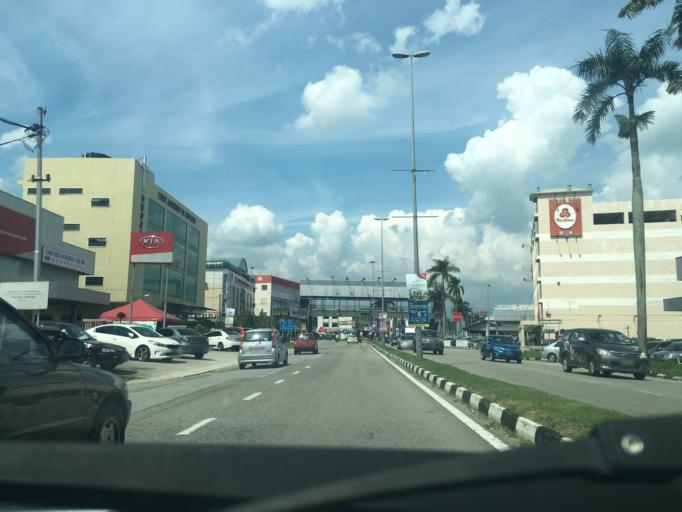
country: MY
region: Perak
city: Ipoh
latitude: 4.5845
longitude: 101.0899
